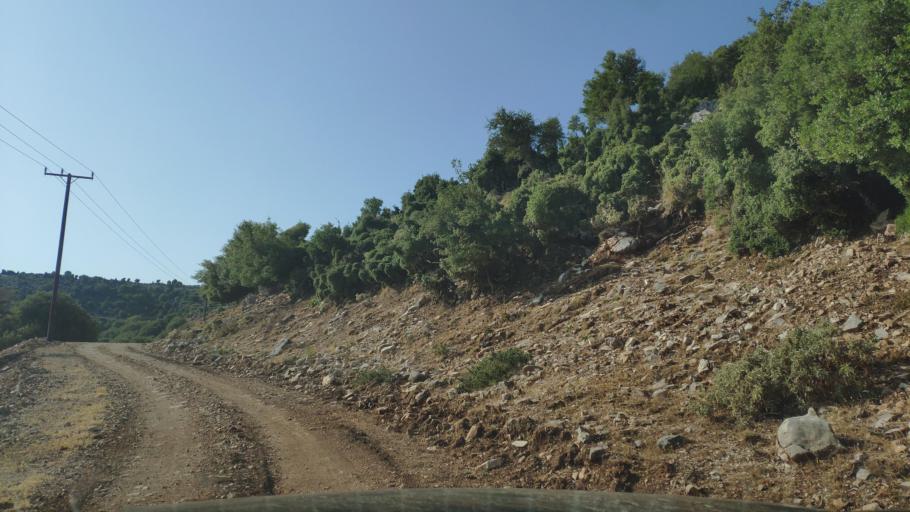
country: GR
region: West Greece
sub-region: Nomos Aitolias kai Akarnanias
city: Monastirakion
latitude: 38.8331
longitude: 20.9719
